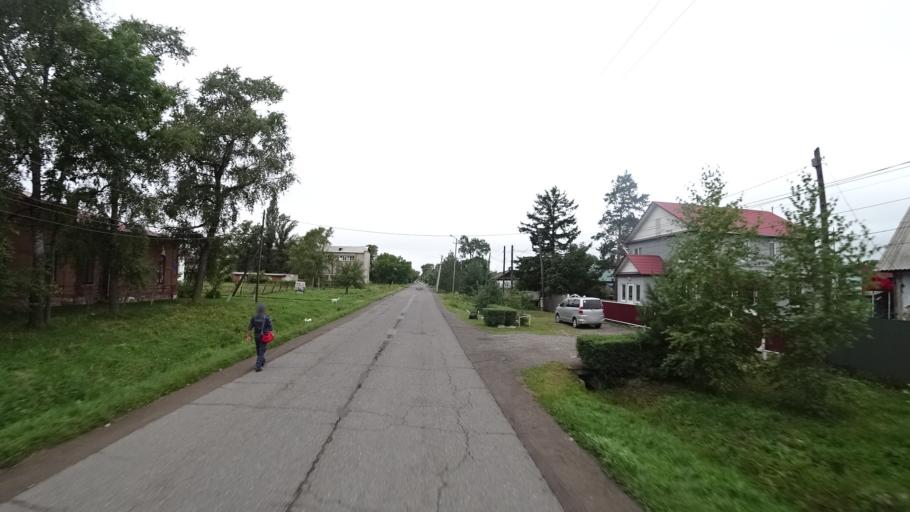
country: RU
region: Primorskiy
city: Chernigovka
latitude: 44.3380
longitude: 132.5794
